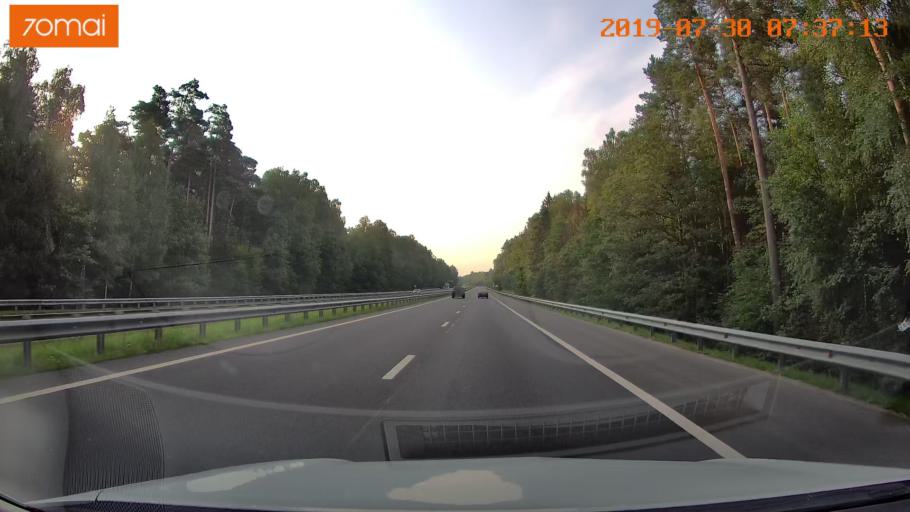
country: RU
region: Kaliningrad
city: Gvardeysk
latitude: 54.6576
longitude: 21.1417
